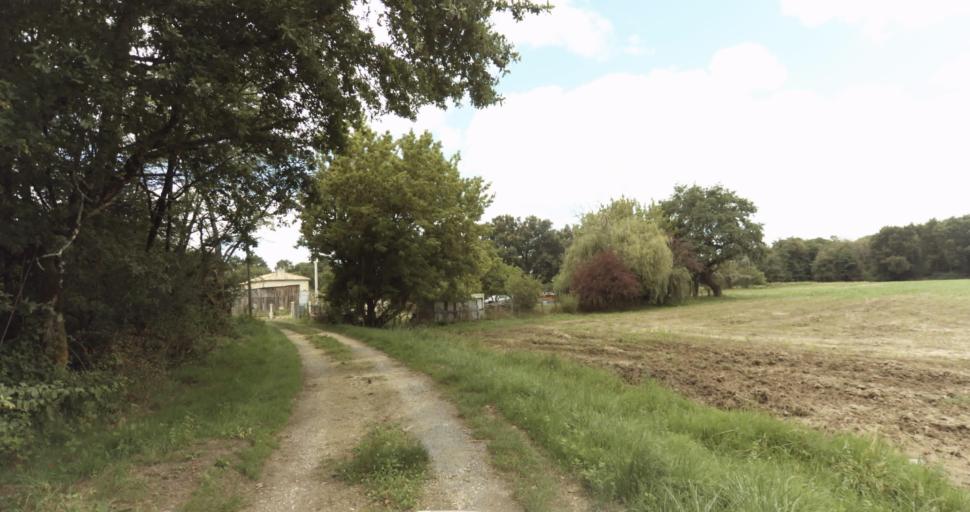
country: FR
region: Aquitaine
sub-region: Departement de la Gironde
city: Bazas
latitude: 44.4664
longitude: -0.2280
